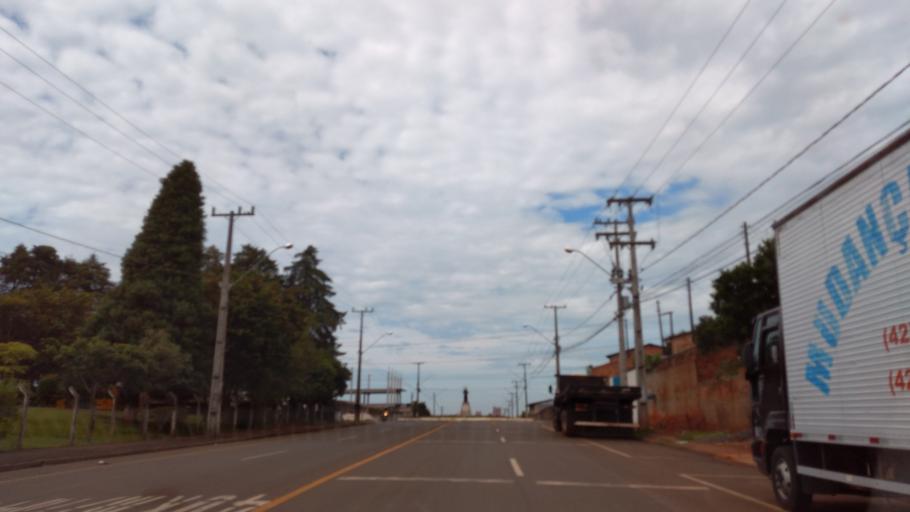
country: BR
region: Parana
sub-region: Guarapuava
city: Guarapuava
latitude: -25.3730
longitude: -51.4434
